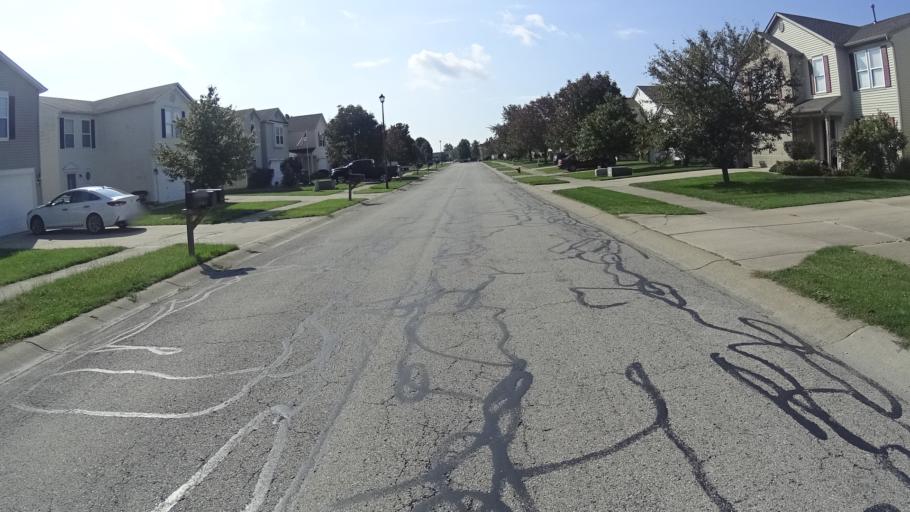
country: US
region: Indiana
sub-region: Madison County
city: Ingalls
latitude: 39.9848
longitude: -85.8471
